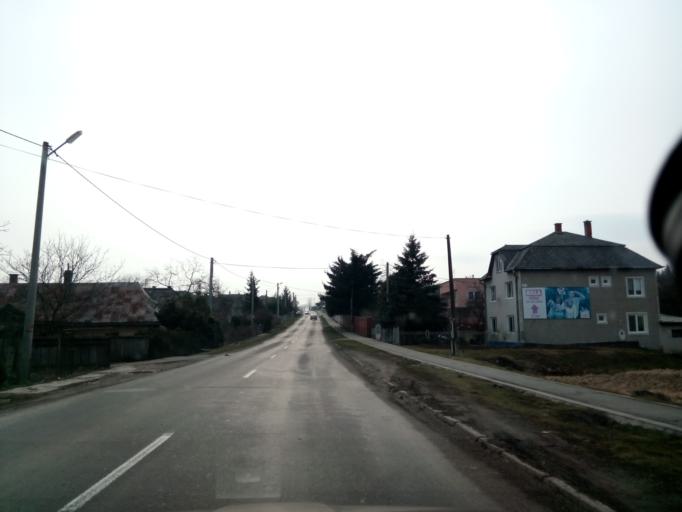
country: SK
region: Kosicky
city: Secovce
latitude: 48.6441
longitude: 21.5699
